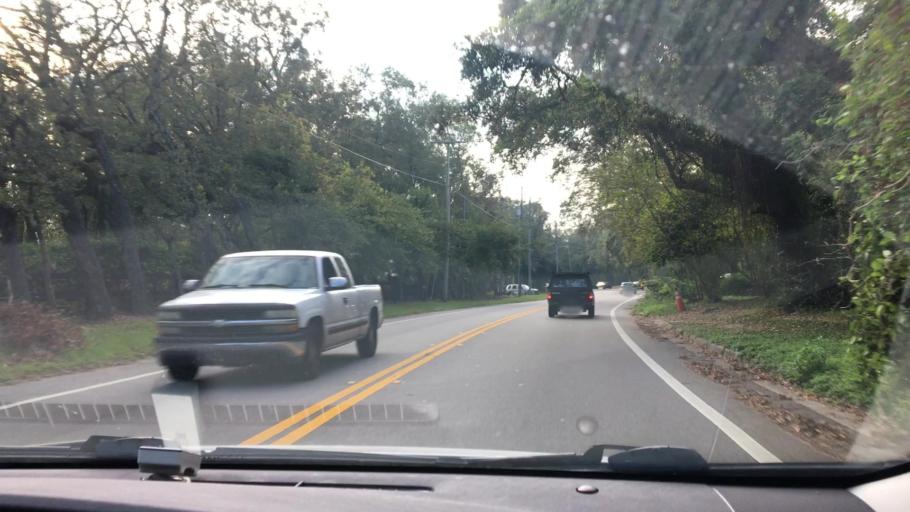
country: US
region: Florida
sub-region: Seminole County
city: Longwood
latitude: 28.7145
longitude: -81.3471
